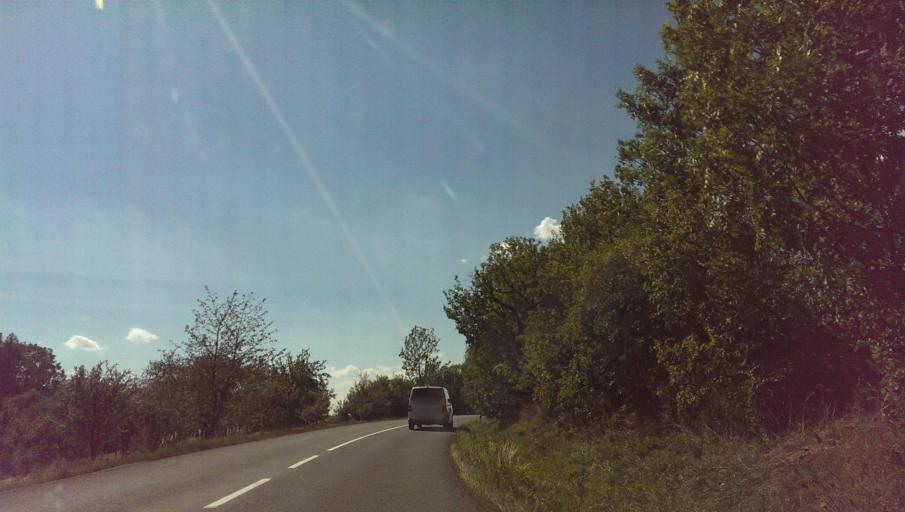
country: CZ
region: Zlin
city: Kelc
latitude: 49.4422
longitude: 17.8451
